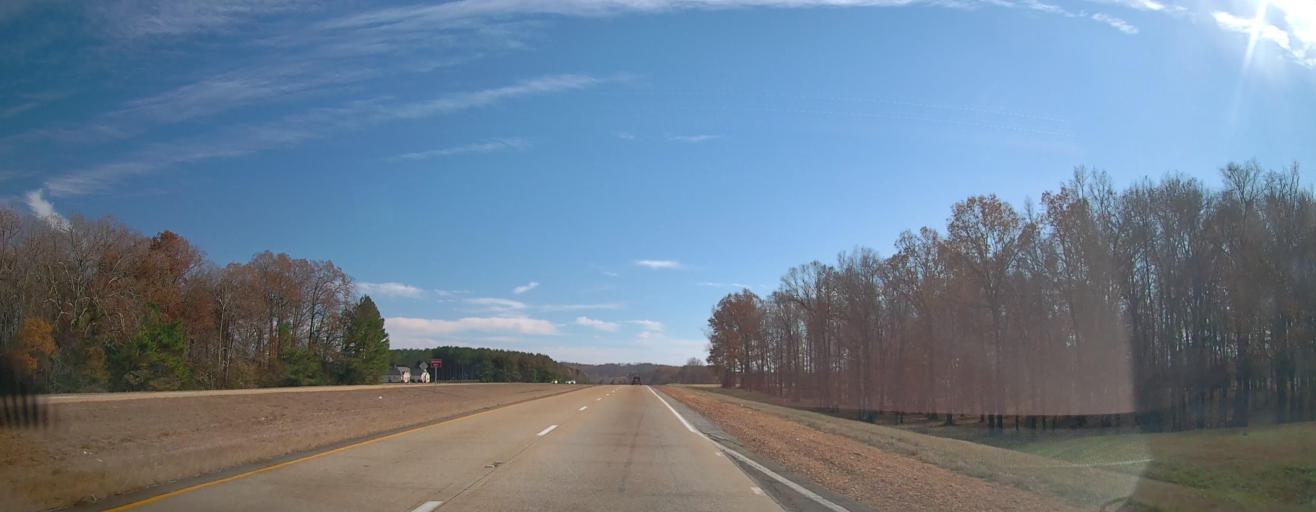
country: US
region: Mississippi
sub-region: Tishomingo County
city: Iuka
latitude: 34.8192
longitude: -88.2905
